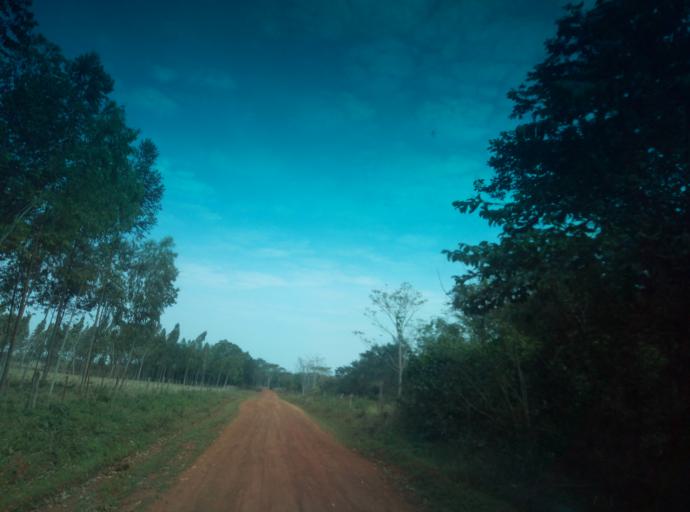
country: PY
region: Caaguazu
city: Carayao
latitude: -25.1951
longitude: -56.2520
